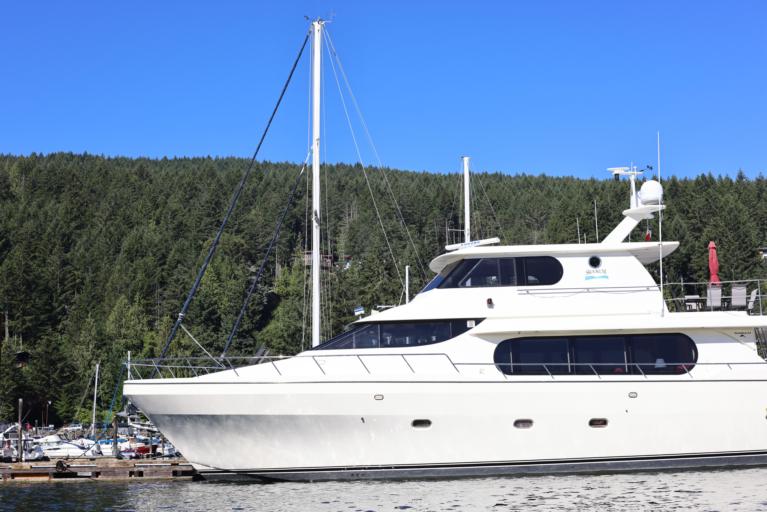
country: CA
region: British Columbia
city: North Cowichan
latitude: 48.7969
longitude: -123.6006
